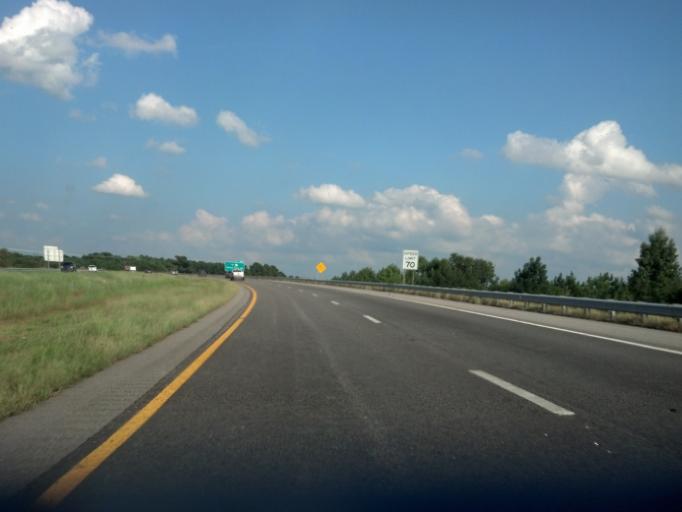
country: US
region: North Carolina
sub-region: Edgecombe County
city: Princeville
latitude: 35.8657
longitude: -77.5138
